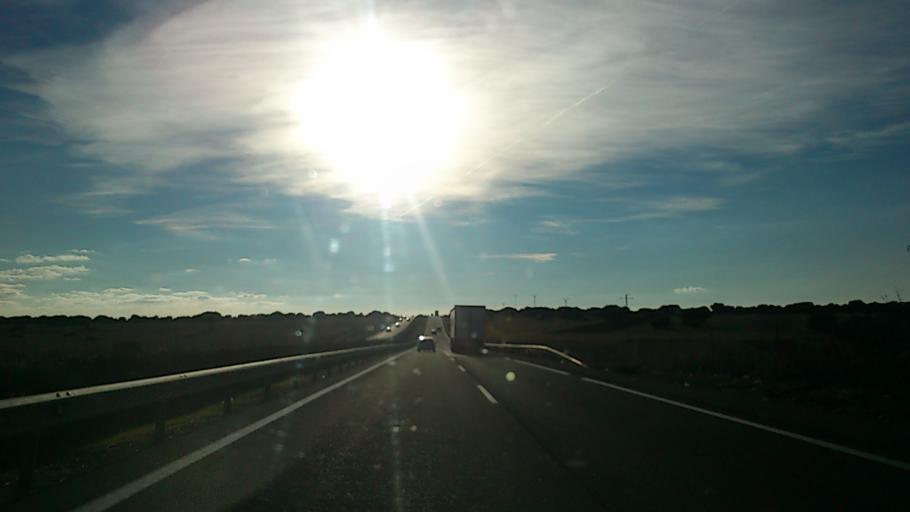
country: ES
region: Castille-La Mancha
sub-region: Provincia de Guadalajara
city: Algora
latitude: 40.9457
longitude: -2.6928
